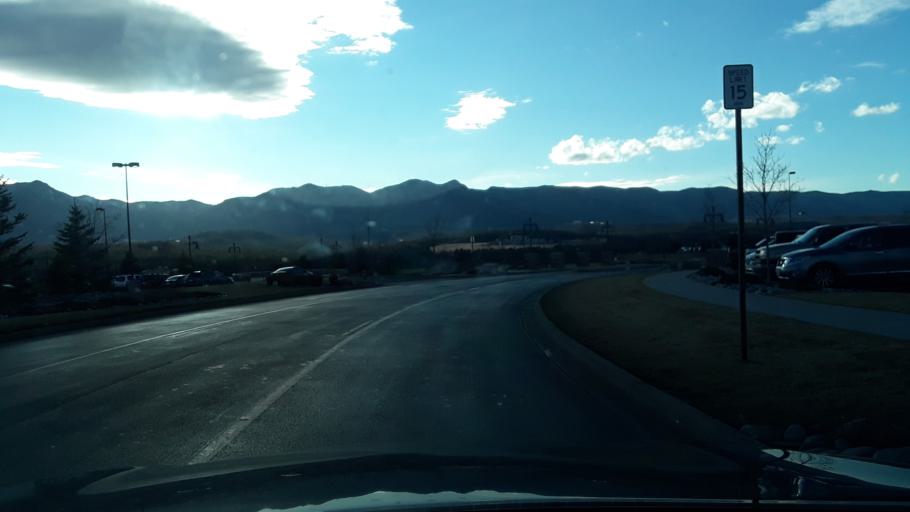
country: US
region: Colorado
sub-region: El Paso County
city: Air Force Academy
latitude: 38.9921
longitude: -104.8087
